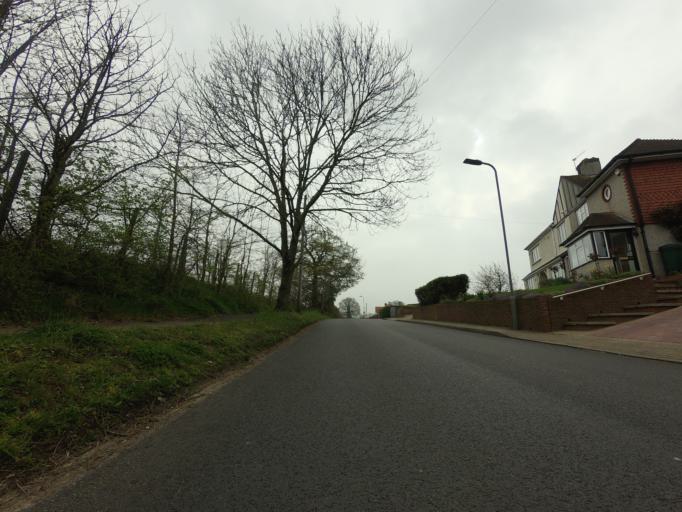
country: GB
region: England
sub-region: Greater London
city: Orpington
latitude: 51.3828
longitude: 0.1202
